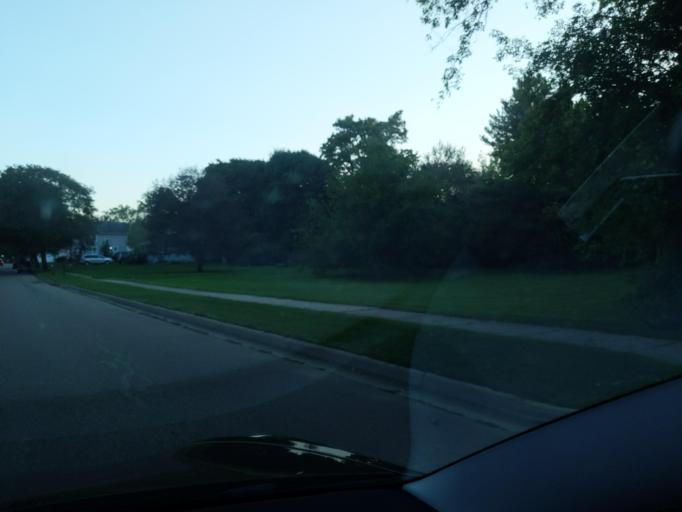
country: US
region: Michigan
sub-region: Jackson County
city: Jackson
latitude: 42.2584
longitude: -84.3844
